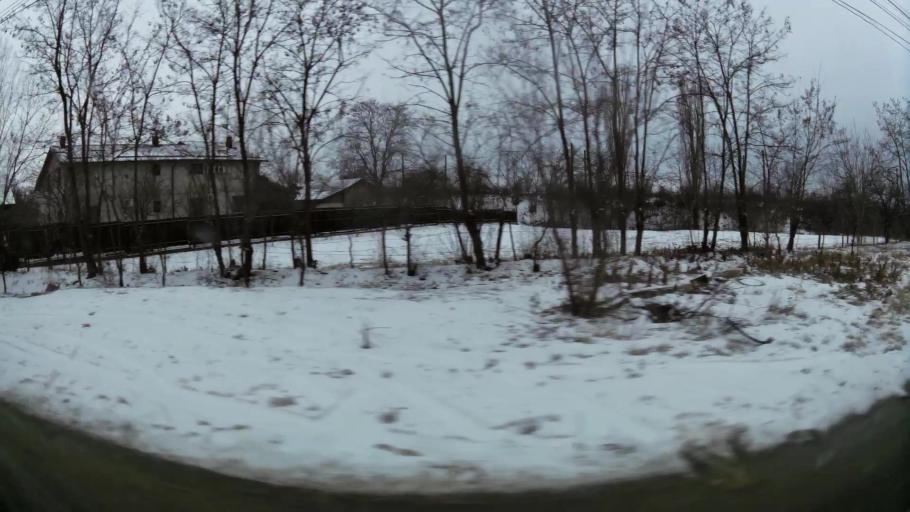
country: RO
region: Prahova
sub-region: Comuna Berceni
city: Corlatesti
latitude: 44.9193
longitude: 26.0817
